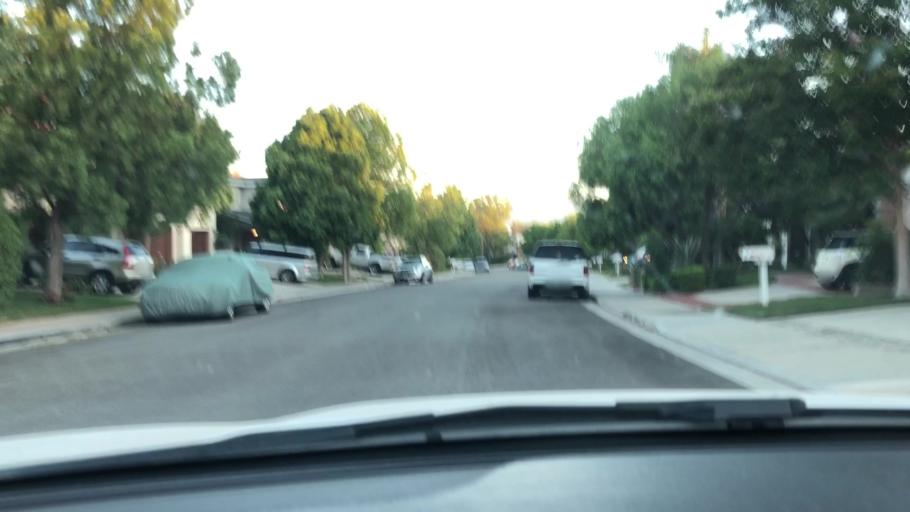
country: US
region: California
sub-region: Los Angeles County
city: Santa Clarita
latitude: 34.4587
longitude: -118.5438
